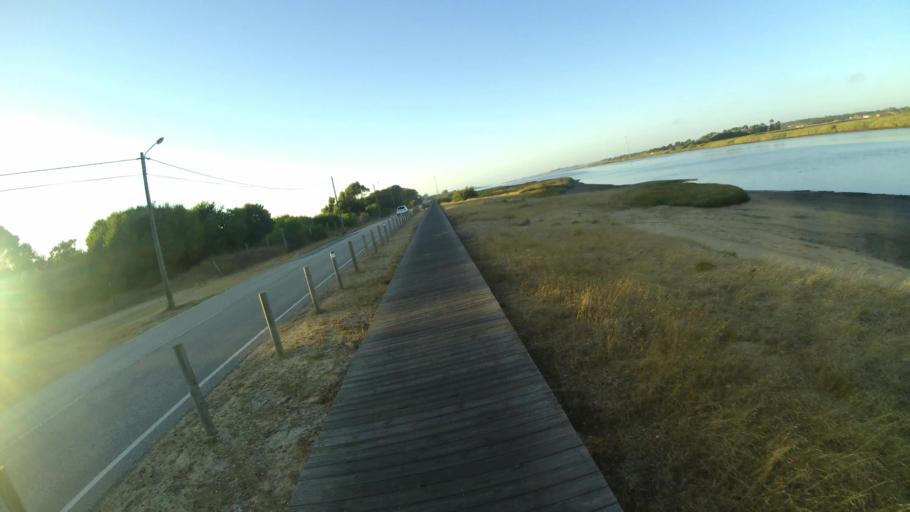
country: PT
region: Aveiro
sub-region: Ilhavo
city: Gafanha da Encarnacao
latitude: 40.5656
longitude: -8.7570
